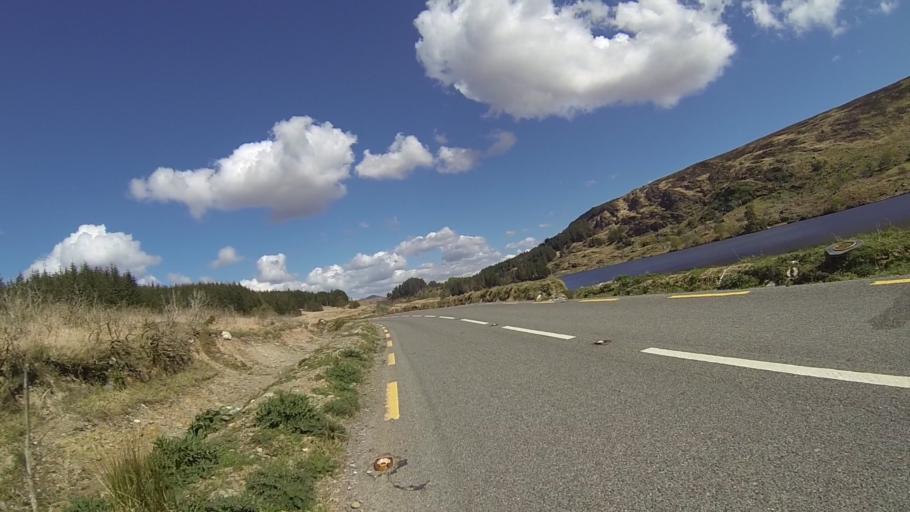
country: IE
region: Munster
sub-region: Ciarrai
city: Kenmare
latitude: 51.9576
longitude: -9.6205
